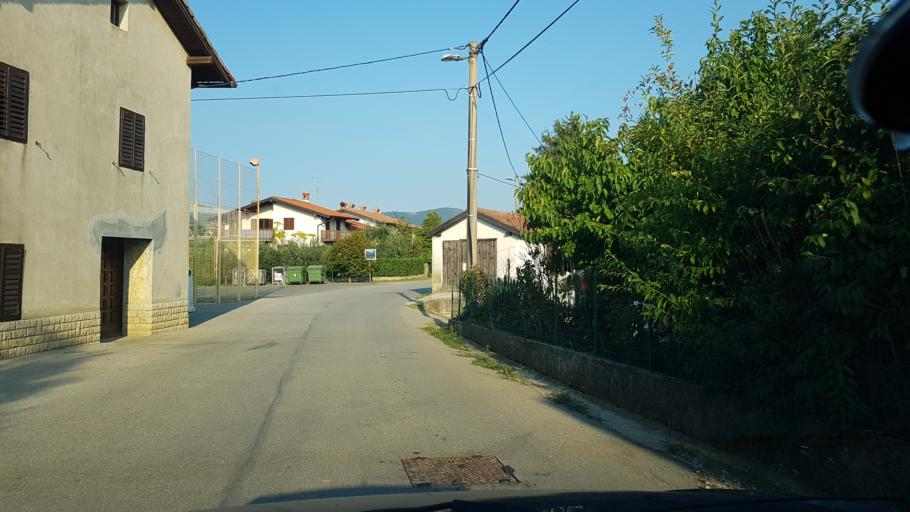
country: IT
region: Friuli Venezia Giulia
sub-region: Provincia di Gorizia
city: San Floriano del Collio
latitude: 45.9828
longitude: 13.5658
